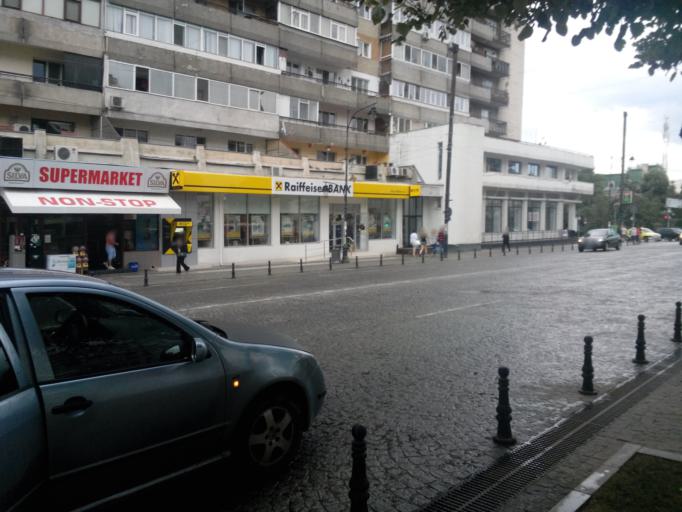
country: RO
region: Iasi
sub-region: Municipiul Iasi
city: Iasi
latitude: 47.1630
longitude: 27.5823
